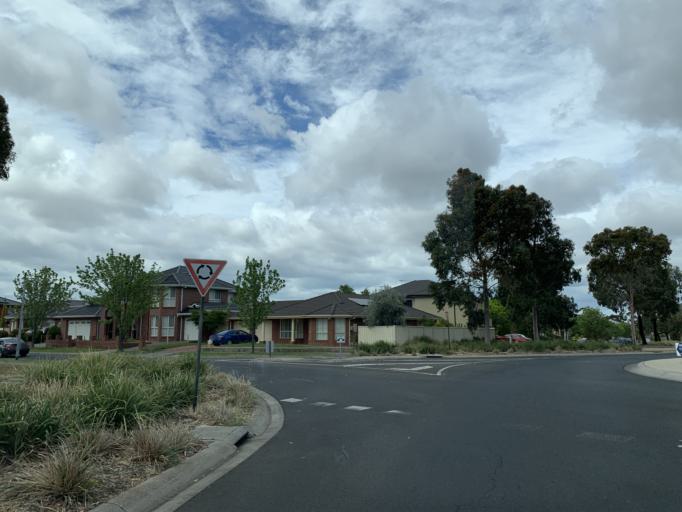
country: AU
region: Victoria
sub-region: Brimbank
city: Cairnlea
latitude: -37.7607
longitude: 144.7903
